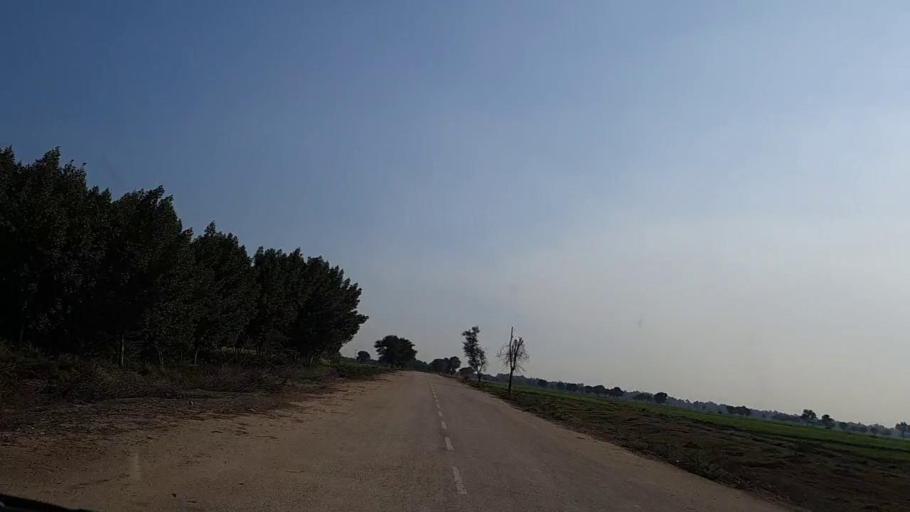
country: PK
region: Sindh
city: Sakrand
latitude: 26.1226
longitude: 68.2482
